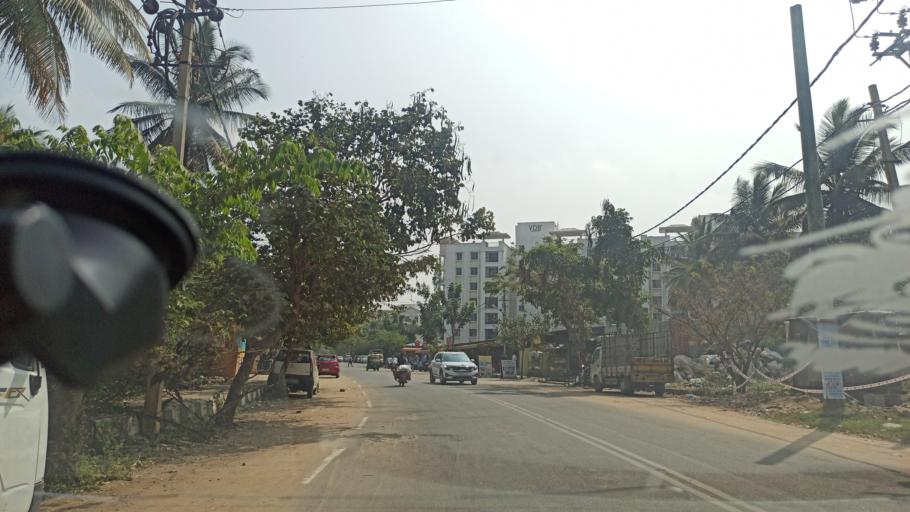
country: IN
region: Karnataka
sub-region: Bangalore Urban
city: Yelahanka
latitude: 13.0920
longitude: 77.6013
